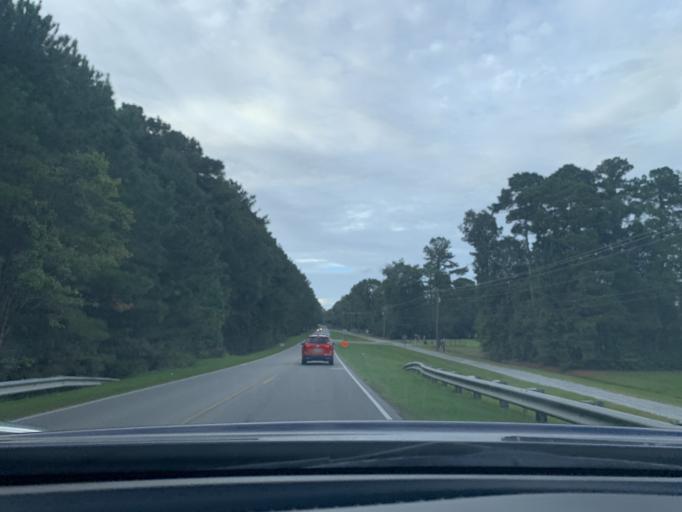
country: US
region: Georgia
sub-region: Chatham County
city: Georgetown
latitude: 32.0441
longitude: -81.2626
